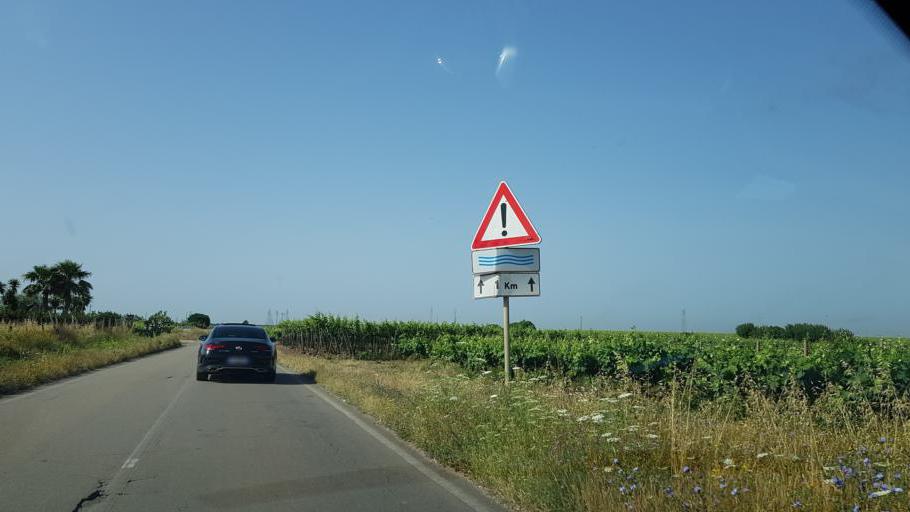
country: IT
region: Apulia
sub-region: Provincia di Brindisi
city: San Pancrazio Salentino
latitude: 40.3991
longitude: 17.8351
